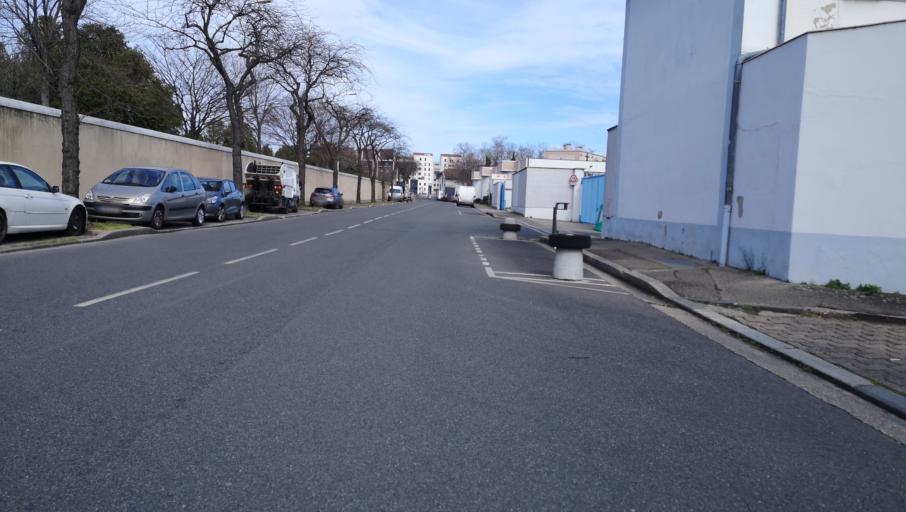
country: FR
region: Rhone-Alpes
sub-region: Departement du Rhone
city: Lyon
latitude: 45.7365
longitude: 4.8577
